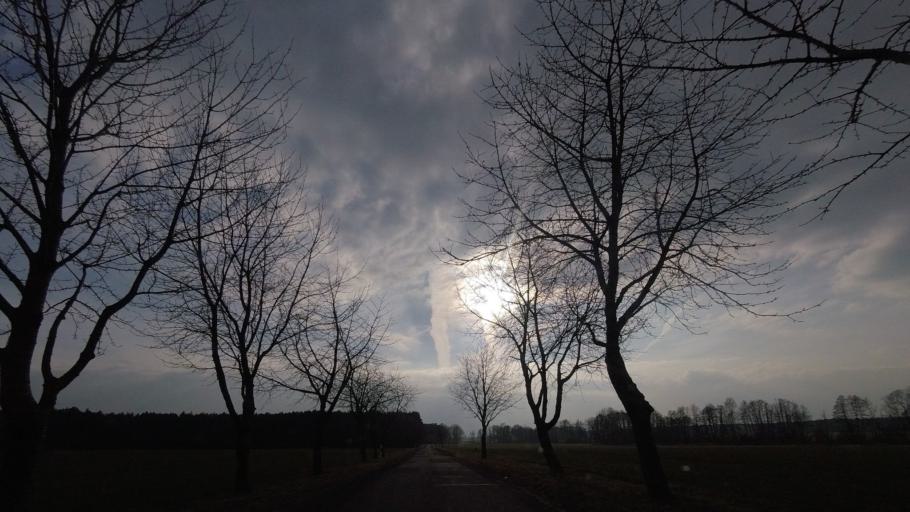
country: DE
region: Brandenburg
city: Belzig
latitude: 52.1617
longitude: 12.6763
